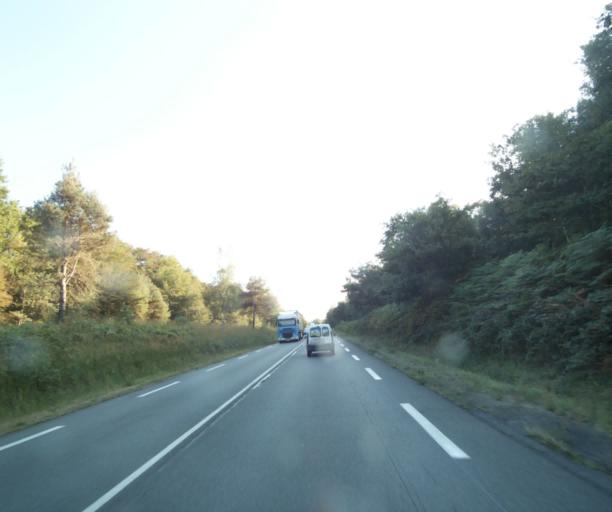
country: FR
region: Bourgogne
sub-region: Departement de Saone-et-Loire
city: Palinges
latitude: 46.5363
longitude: 4.1699
